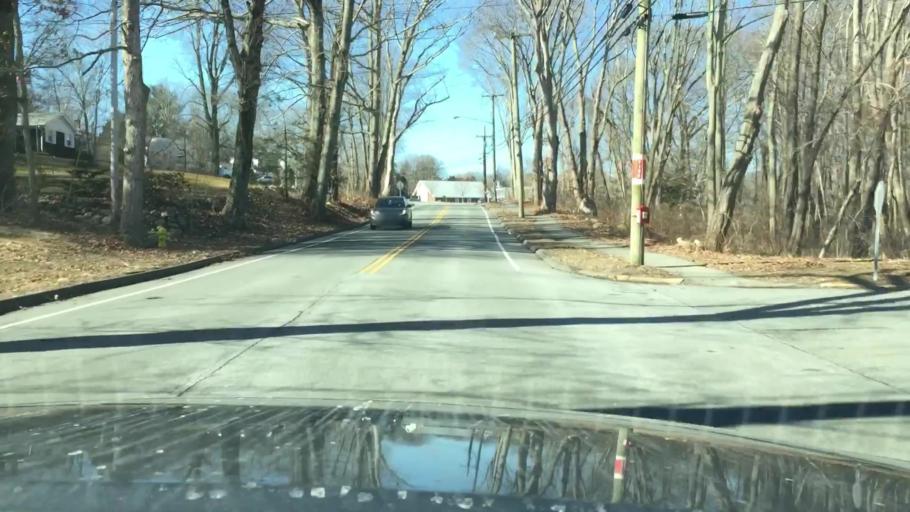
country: US
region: Connecticut
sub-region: New London County
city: Conning Towers-Nautilus Park
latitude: 41.3719
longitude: -72.0659
